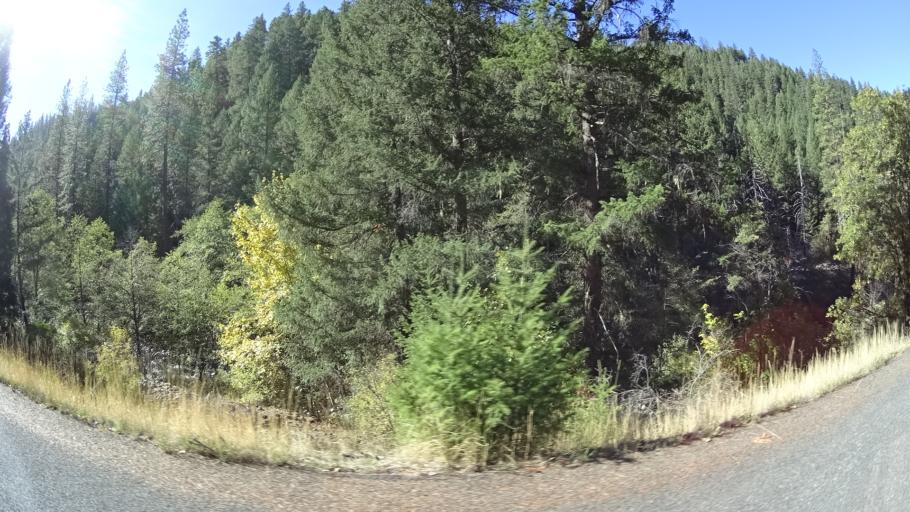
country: US
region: California
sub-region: Trinity County
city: Weaverville
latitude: 41.1463
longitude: -123.1063
